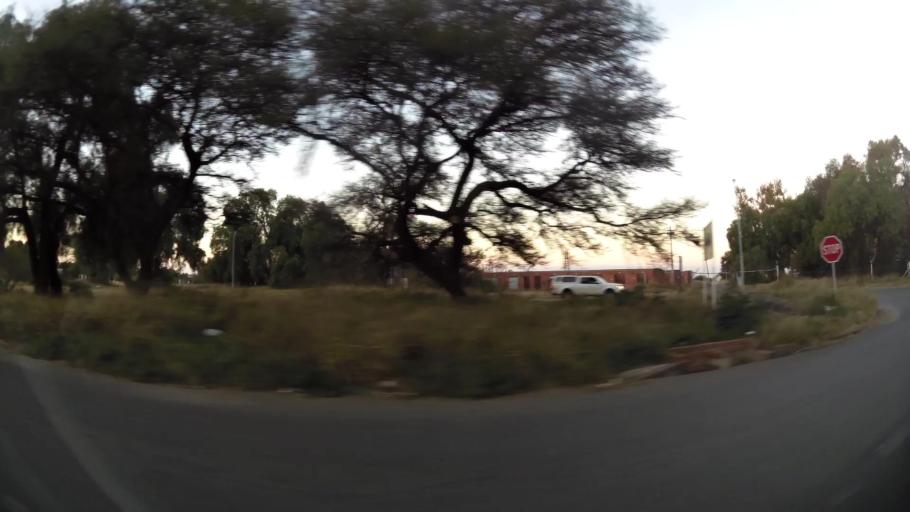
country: ZA
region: Northern Cape
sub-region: Frances Baard District Municipality
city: Kimberley
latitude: -28.7246
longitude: 24.7756
